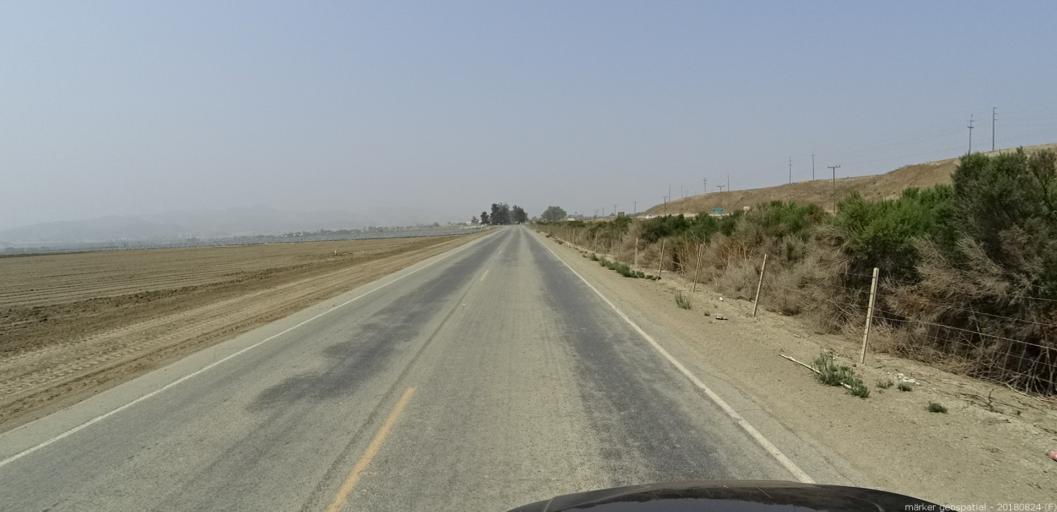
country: US
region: California
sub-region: Monterey County
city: King City
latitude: 36.1979
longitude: -121.1038
